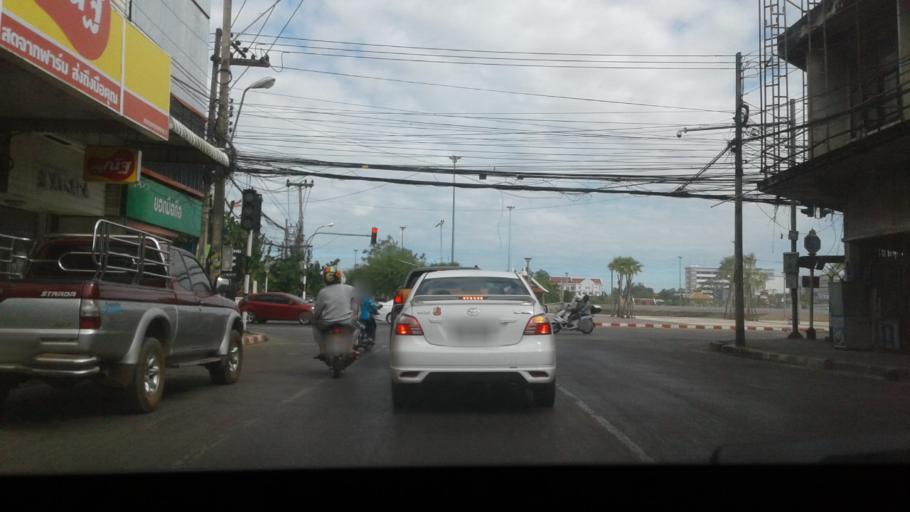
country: TH
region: Changwat Udon Thani
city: Udon Thani
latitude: 17.4091
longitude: 102.7843
